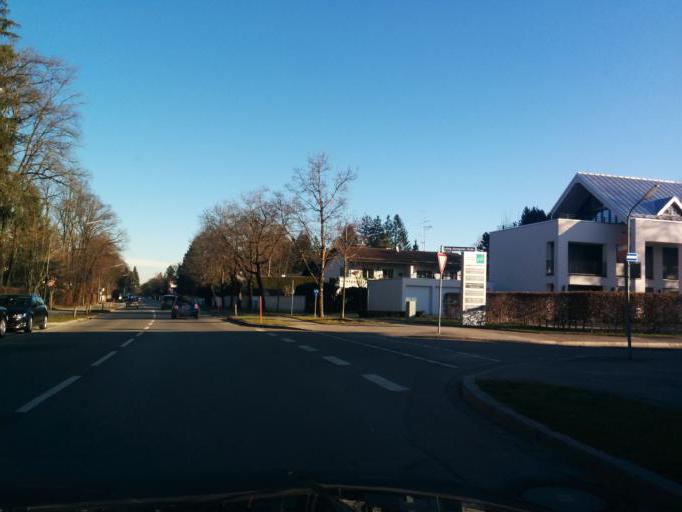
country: DE
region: Bavaria
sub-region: Upper Bavaria
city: Grunwald
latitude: 48.0482
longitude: 11.5317
